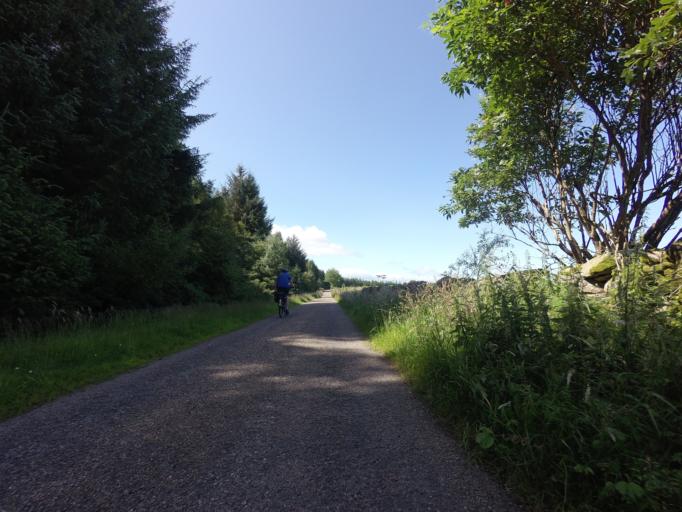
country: GB
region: Scotland
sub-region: Highland
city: Nairn
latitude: 57.5099
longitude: -3.8938
